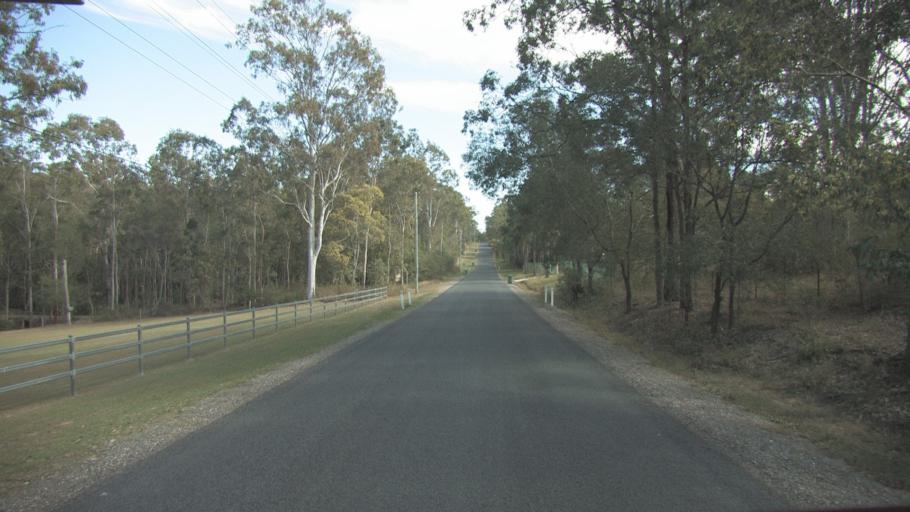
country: AU
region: Queensland
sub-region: Logan
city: North Maclean
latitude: -27.7731
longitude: 152.9737
